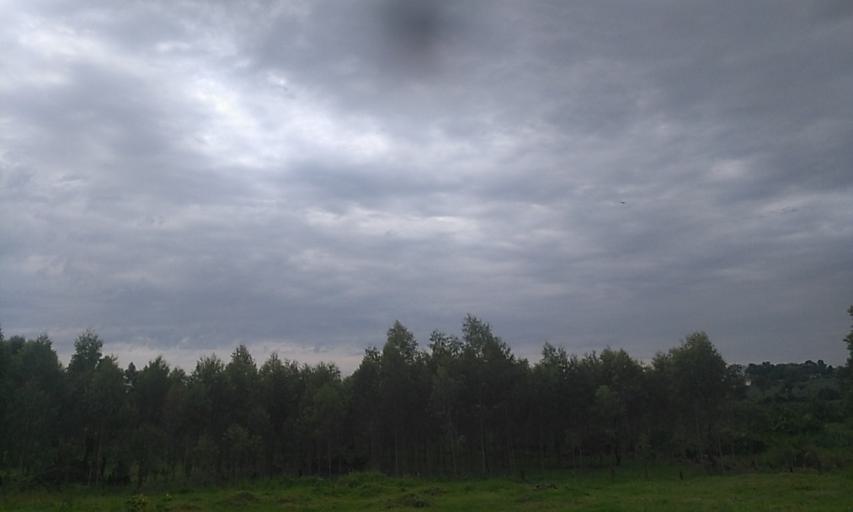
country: UG
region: Central Region
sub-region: Wakiso District
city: Bweyogerere
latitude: 0.3973
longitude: 32.6747
